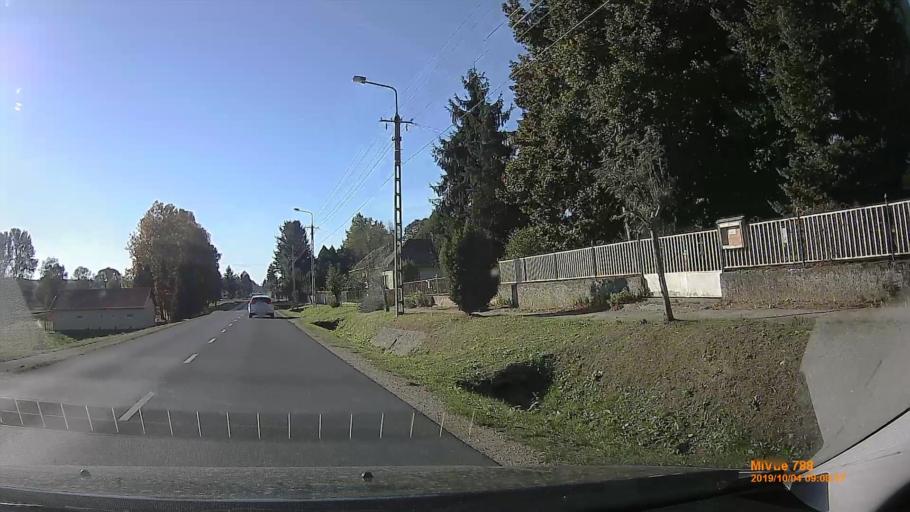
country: HU
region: Somogy
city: Karad
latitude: 46.6719
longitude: 17.7770
